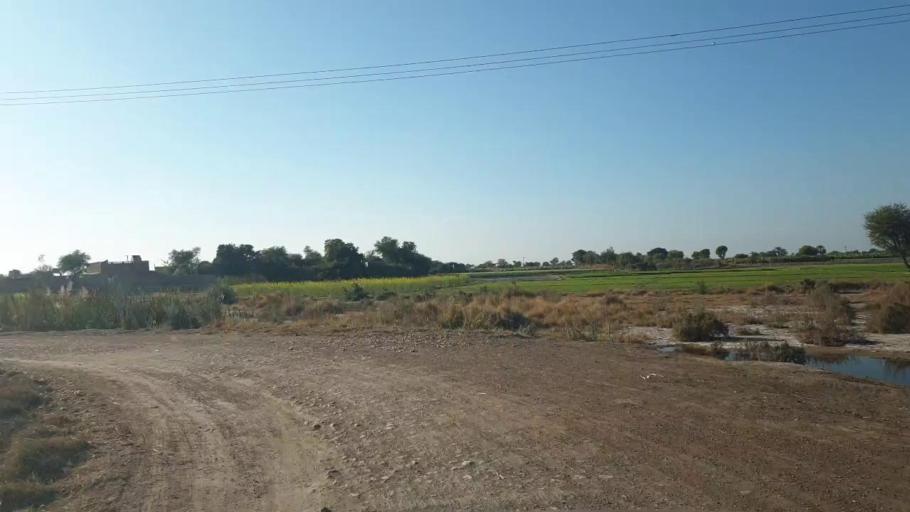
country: PK
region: Sindh
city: Shahdadpur
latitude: 25.9295
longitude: 68.5938
